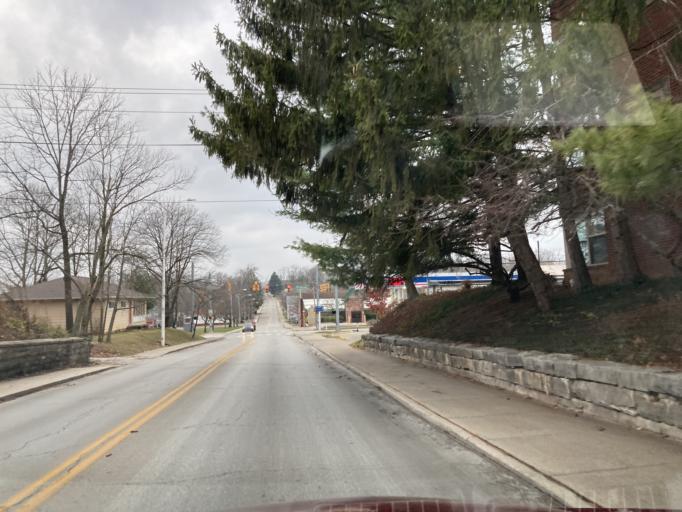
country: US
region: Indiana
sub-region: Monroe County
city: Bloomington
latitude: 39.1717
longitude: -86.5260
